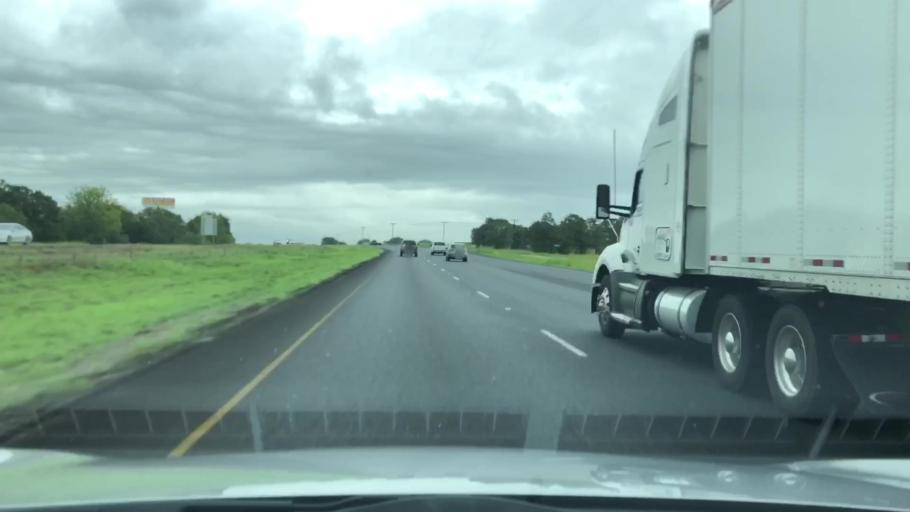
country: US
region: Texas
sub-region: Gonzales County
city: Waelder
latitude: 29.6693
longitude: -97.2989
